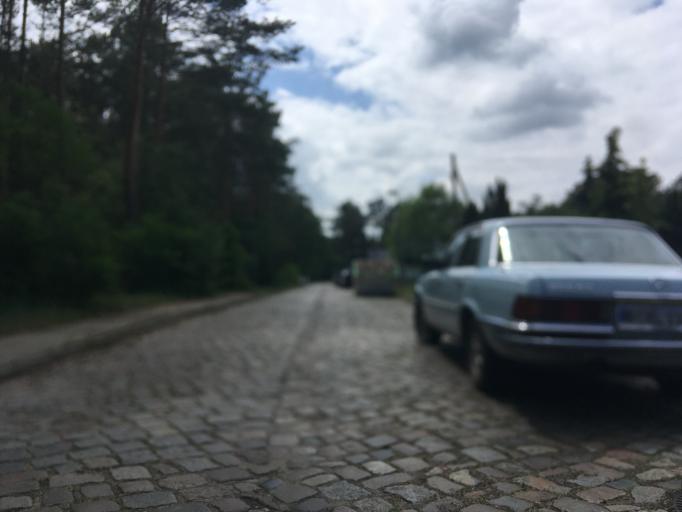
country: DE
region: Berlin
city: Muggelheim
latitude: 52.4066
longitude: 13.6550
